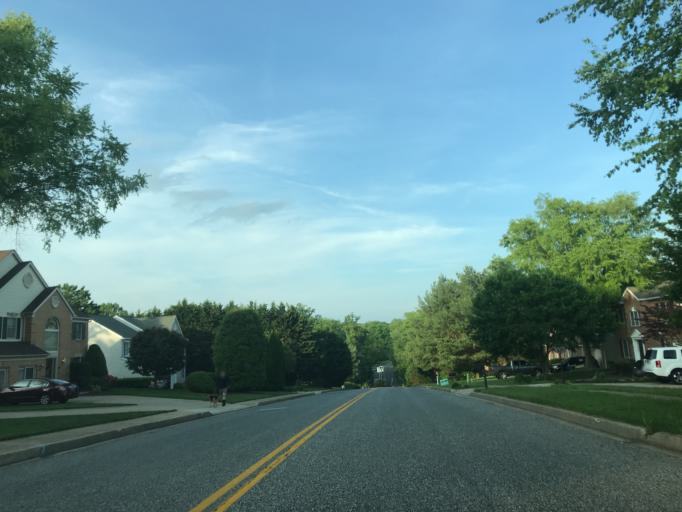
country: US
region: Maryland
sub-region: Harford County
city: North Bel Air
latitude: 39.5552
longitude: -76.3480
